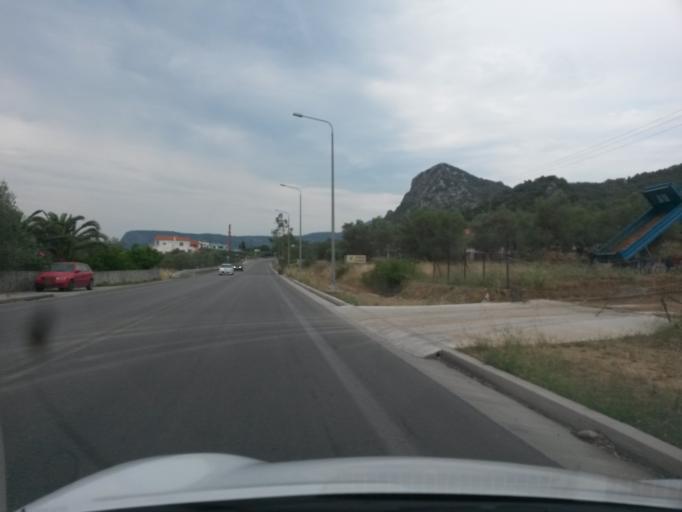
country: GR
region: North Aegean
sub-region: Nomos Lesvou
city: Moria
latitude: 39.1082
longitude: 26.5073
